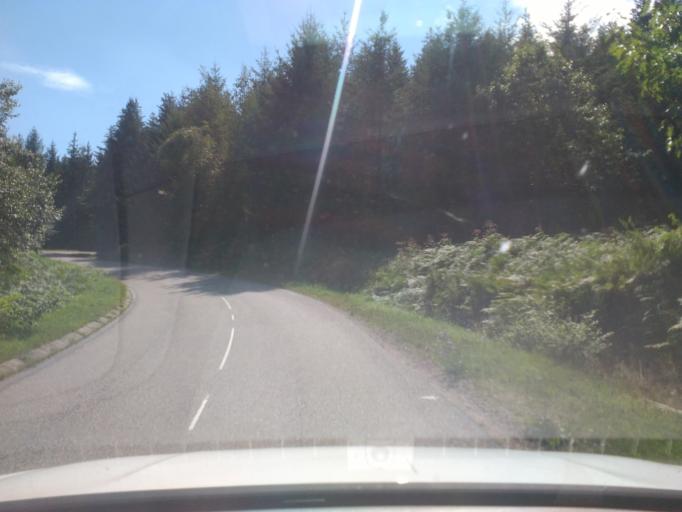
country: FR
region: Lorraine
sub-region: Departement des Vosges
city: Senones
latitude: 48.3693
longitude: 6.9732
